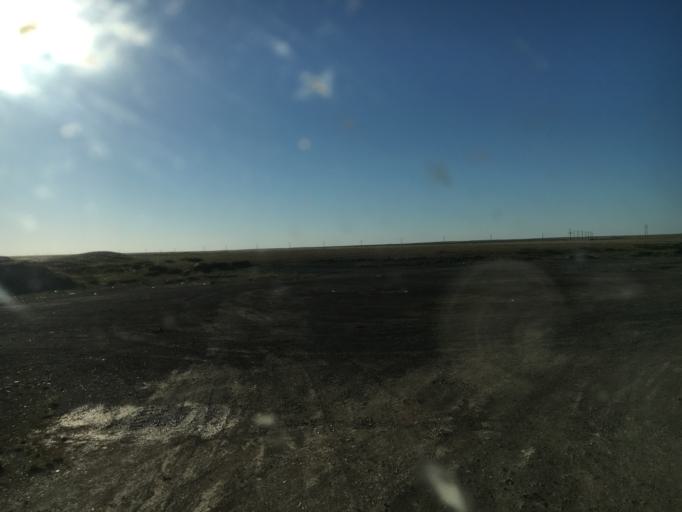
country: KZ
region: Aqtoebe
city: Khromtau
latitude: 50.2527
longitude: 58.3705
